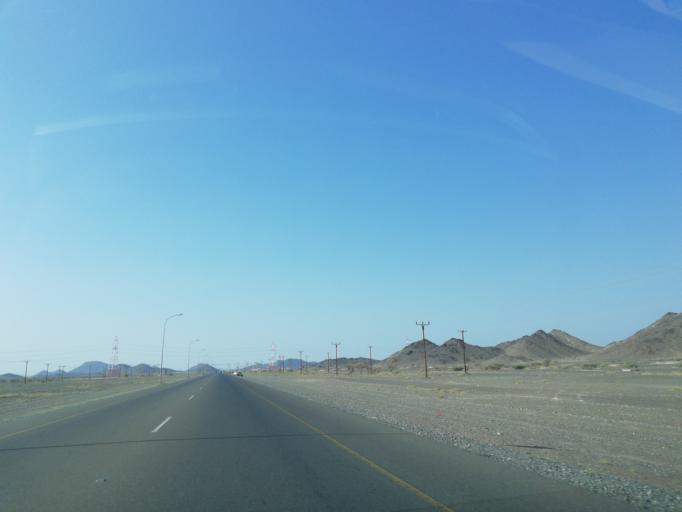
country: OM
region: Ash Sharqiyah
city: Ibra'
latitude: 22.7526
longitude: 58.1477
